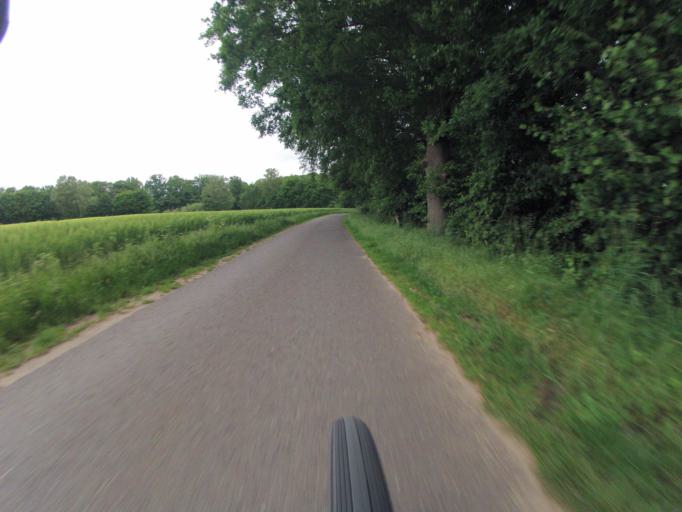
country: DE
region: North Rhine-Westphalia
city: Emsdetten
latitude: 52.2245
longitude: 7.5171
